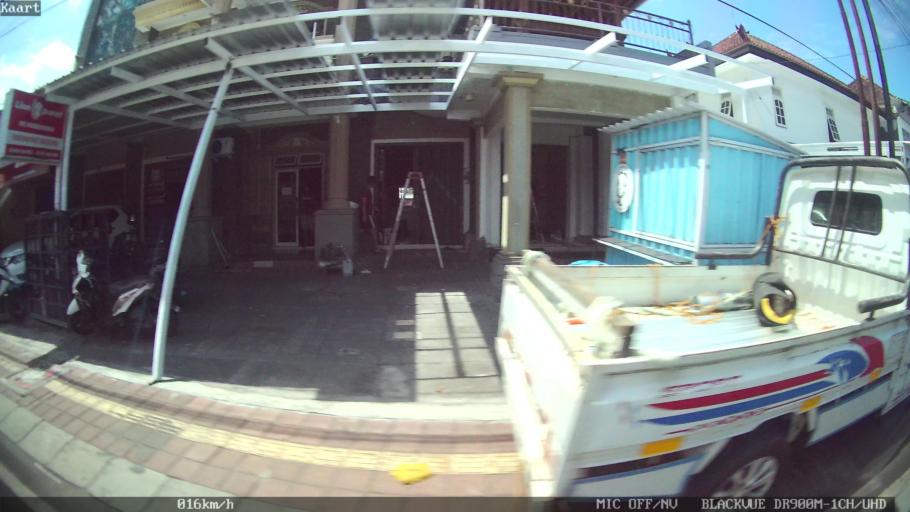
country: ID
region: Bali
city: Denpasar
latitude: -8.6630
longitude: 115.1875
